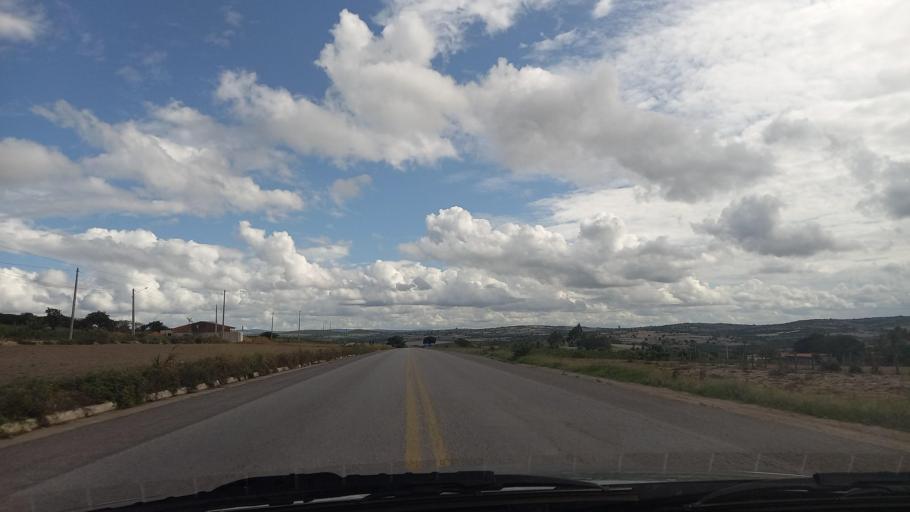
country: BR
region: Pernambuco
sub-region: Lajedo
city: Lajedo
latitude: -8.7216
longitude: -36.4263
